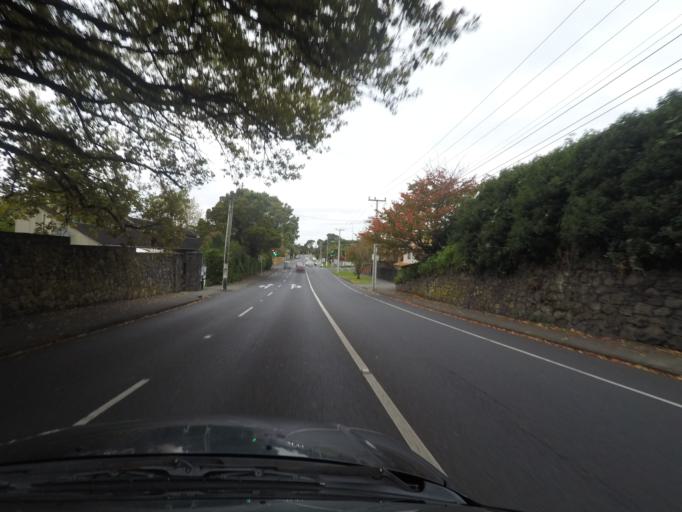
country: NZ
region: Auckland
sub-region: Auckland
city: Auckland
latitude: -36.8820
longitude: 174.7718
